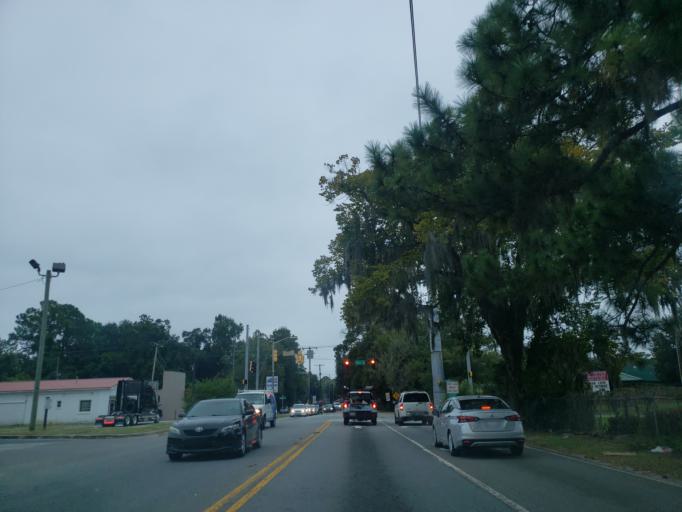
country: US
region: Georgia
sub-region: Chatham County
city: Thunderbolt
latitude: 32.0335
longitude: -81.0681
